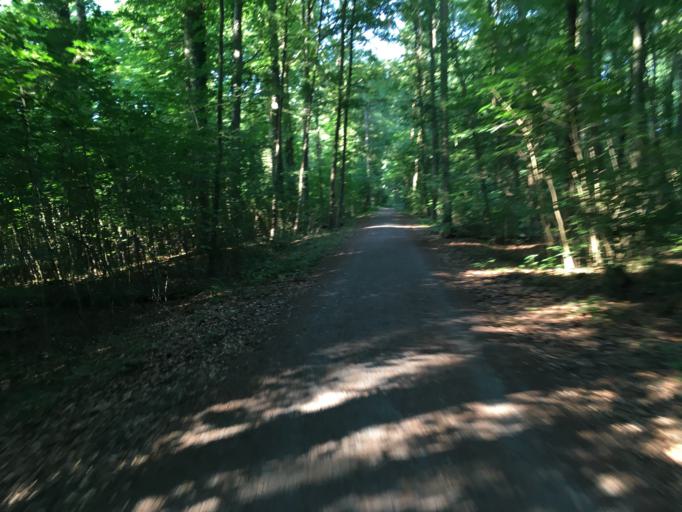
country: DE
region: Hesse
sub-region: Regierungsbezirk Darmstadt
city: Offenbach
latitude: 50.0915
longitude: 8.7246
